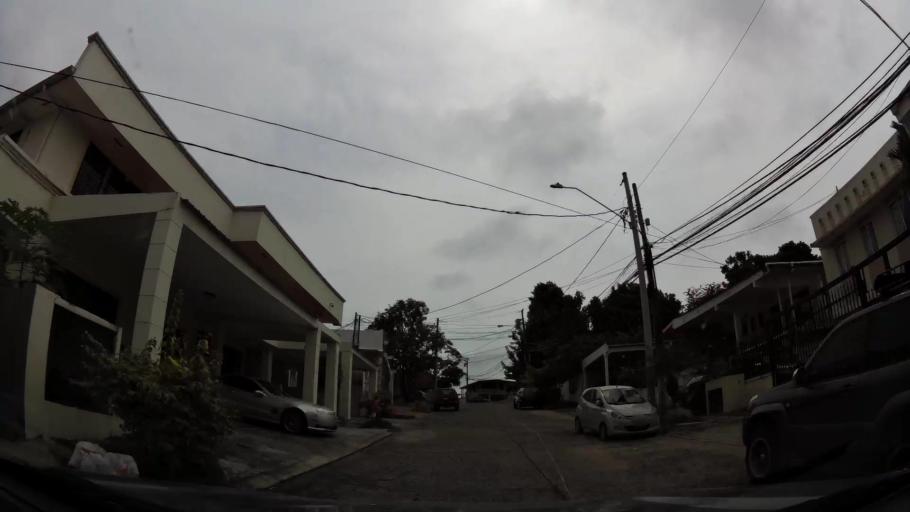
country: PA
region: Panama
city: Panama
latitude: 8.9997
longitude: -79.5302
